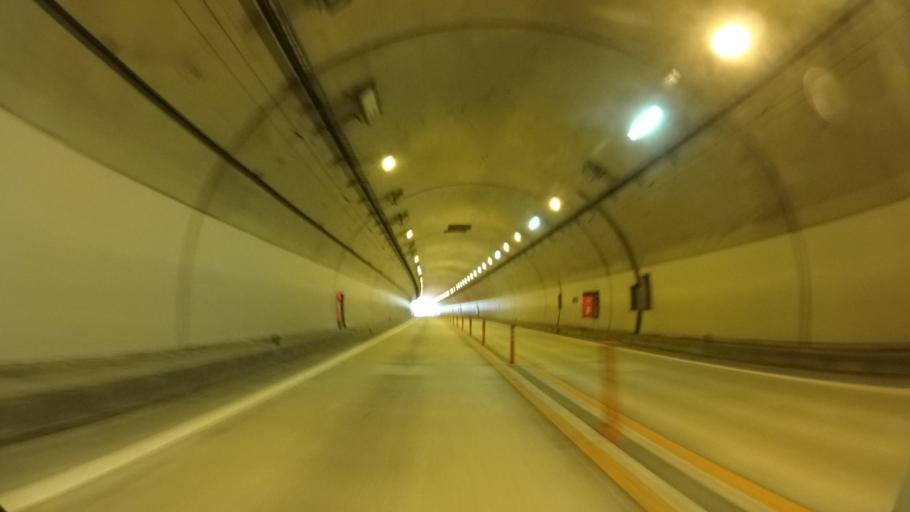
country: JP
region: Hyogo
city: Yamazakicho-nakabirose
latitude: 35.0840
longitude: 134.3429
